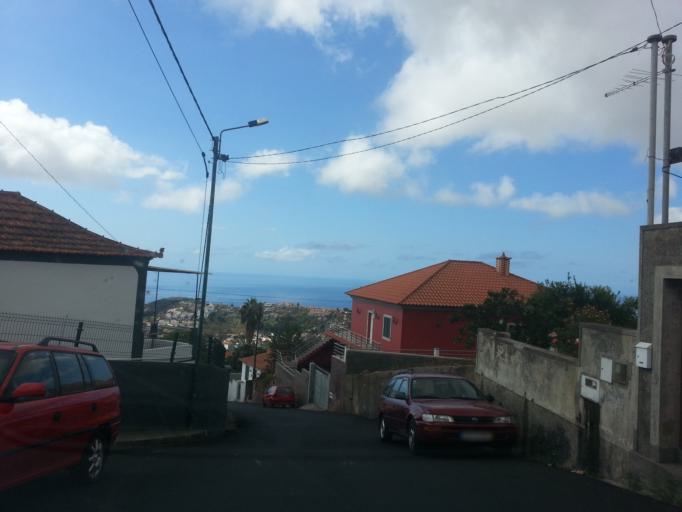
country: PT
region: Madeira
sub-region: Funchal
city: Nossa Senhora do Monte
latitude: 32.6746
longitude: -16.9389
